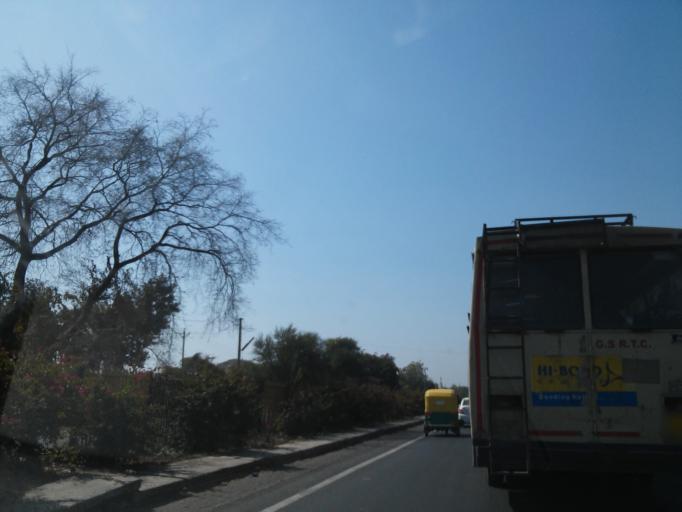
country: IN
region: Gujarat
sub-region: Mahesana
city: Vijapur
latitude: 23.4452
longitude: 72.8573
